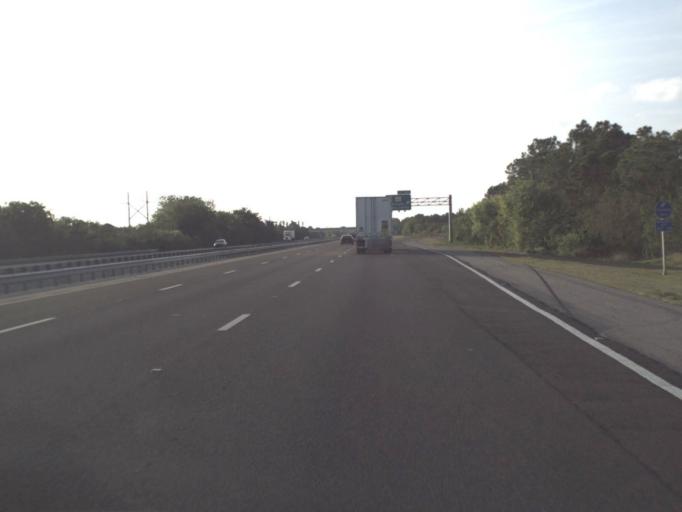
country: US
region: Florida
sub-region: Brevard County
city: Port Saint John
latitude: 28.4958
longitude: -80.8338
